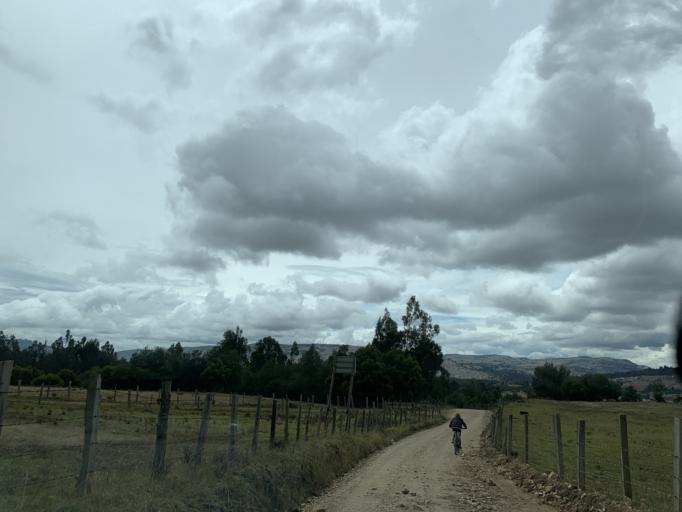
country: CO
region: Boyaca
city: Tunja
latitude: 5.5584
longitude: -73.3248
